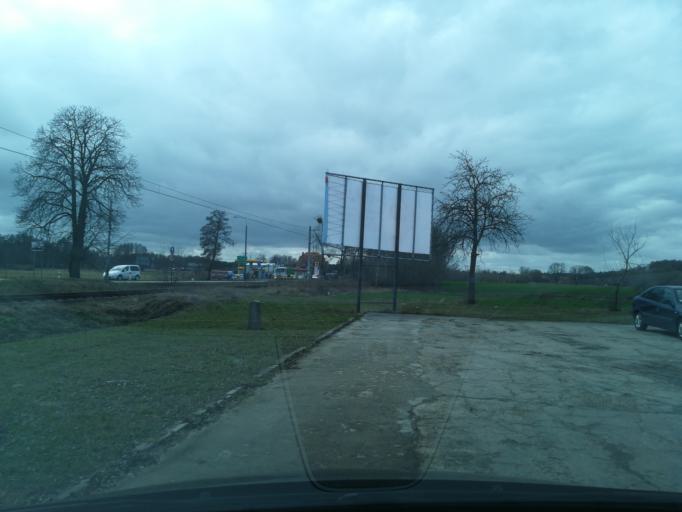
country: PL
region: Kujawsko-Pomorskie
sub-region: Powiat aleksandrowski
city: Ciechocinek
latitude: 52.8759
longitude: 18.7690
